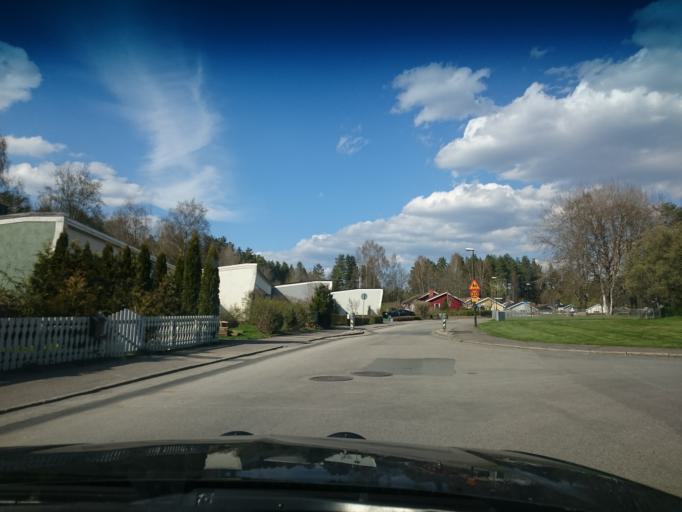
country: SE
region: Joenkoeping
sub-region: Vetlanda Kommun
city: Vetlanda
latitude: 57.4270
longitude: 15.0982
